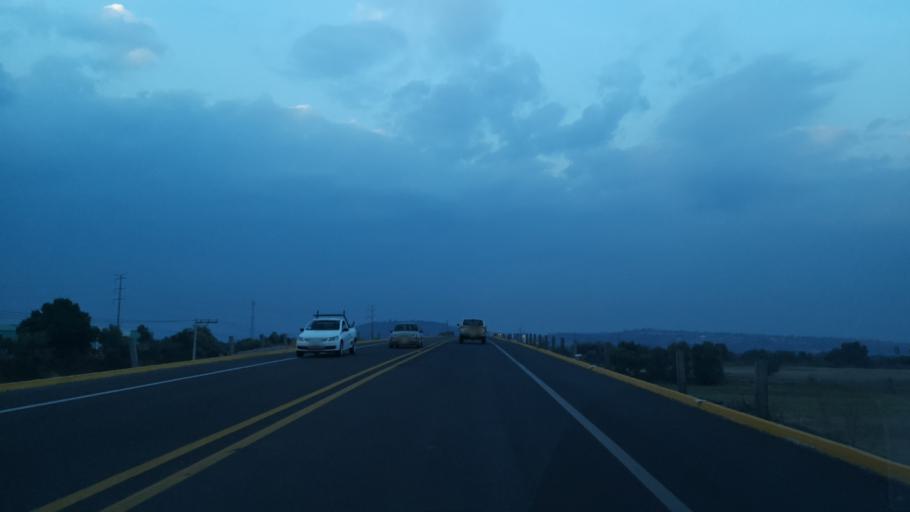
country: MX
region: Puebla
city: Santa Ana Xalmimilulco
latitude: 19.2059
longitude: -98.3615
